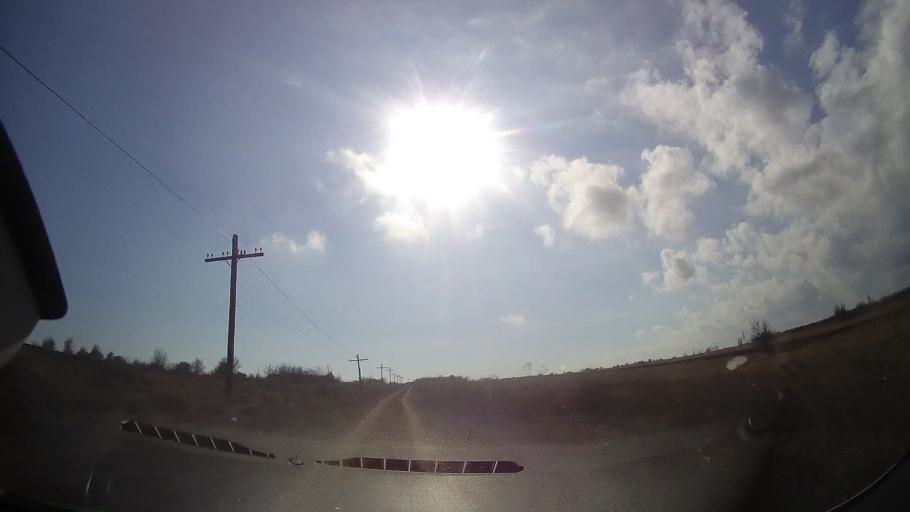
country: RO
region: Constanta
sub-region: Comuna Tuzla
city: Tuzla
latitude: 43.9930
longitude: 28.6452
